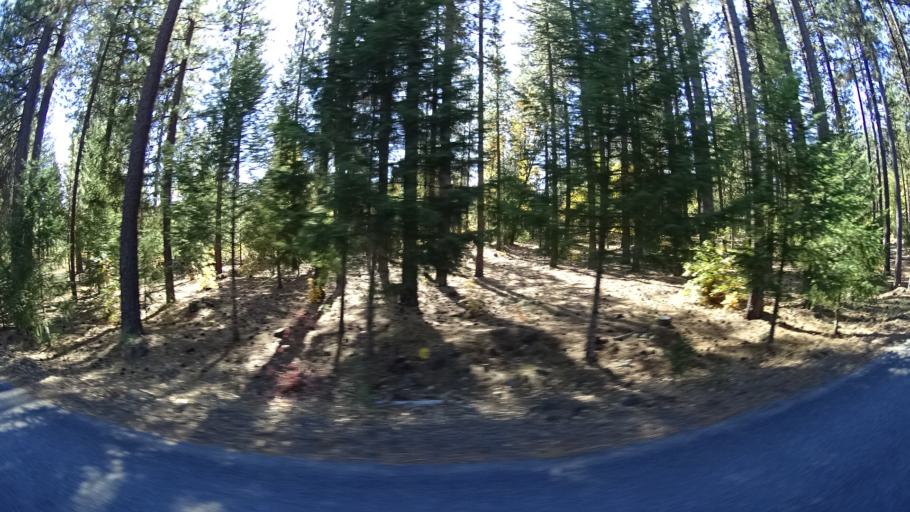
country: US
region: California
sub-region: Siskiyou County
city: Yreka
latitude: 41.5119
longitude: -122.9205
